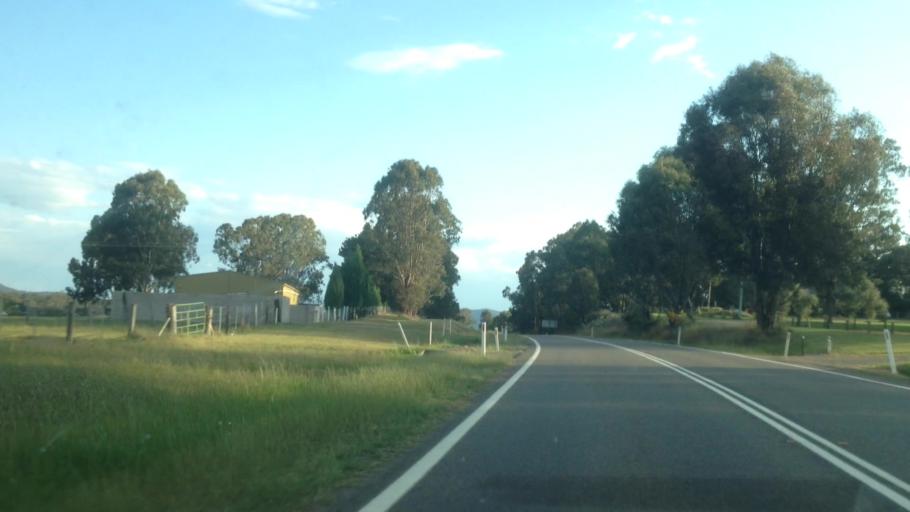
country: AU
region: New South Wales
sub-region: Cessnock
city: Kurri Kurri
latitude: -32.8653
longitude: 151.4802
